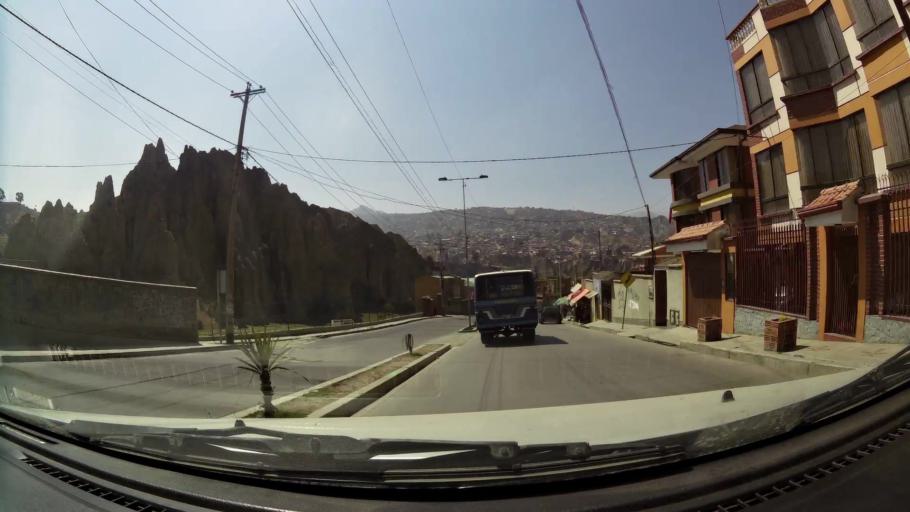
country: BO
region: La Paz
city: La Paz
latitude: -16.5231
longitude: -68.1211
